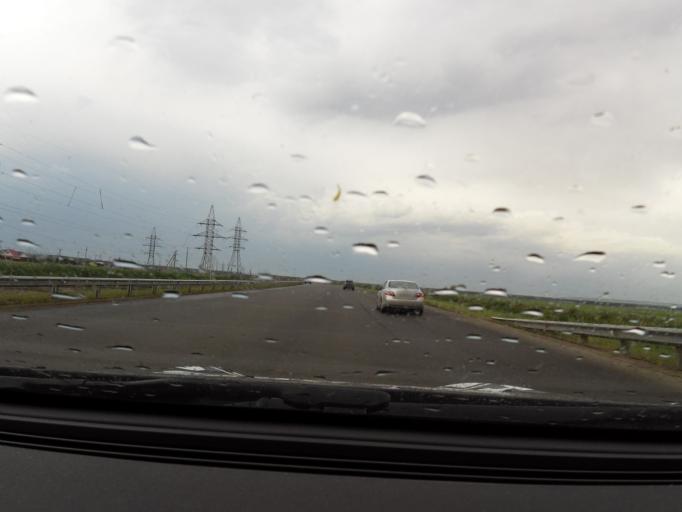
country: RU
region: Bashkortostan
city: Mikhaylovka
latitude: 54.8745
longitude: 55.7306
